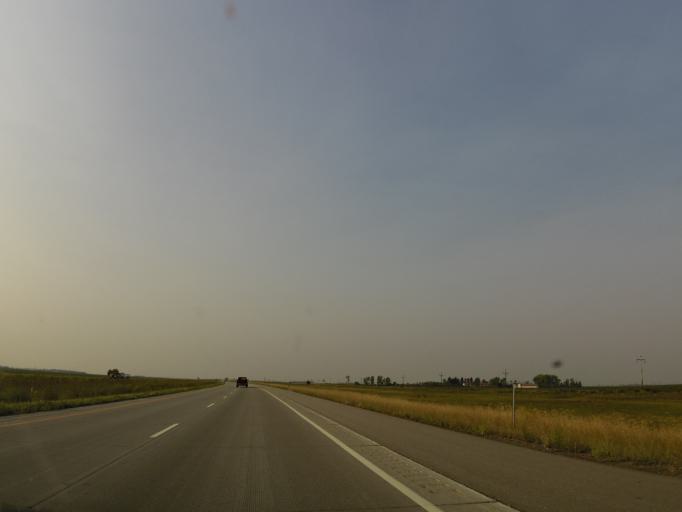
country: US
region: North Dakota
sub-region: Traill County
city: Hillsboro
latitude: 47.1727
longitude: -96.9792
